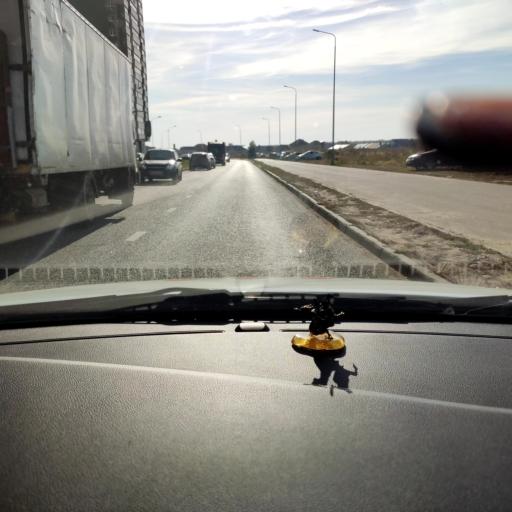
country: RU
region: Tatarstan
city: Osinovo
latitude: 55.8648
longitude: 48.8714
